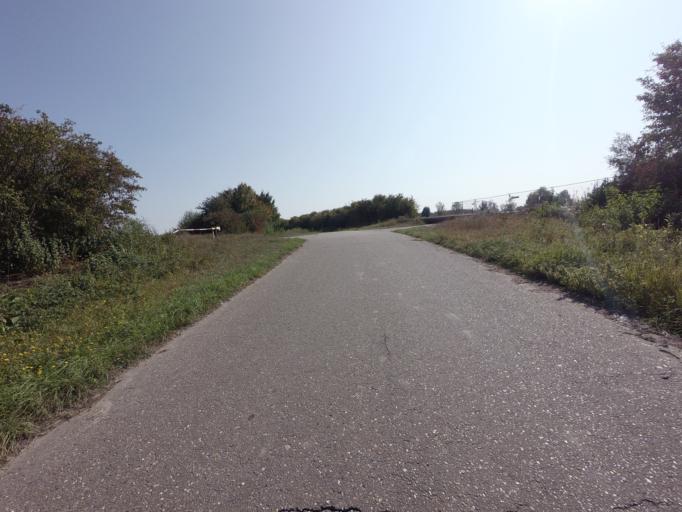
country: NL
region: Limburg
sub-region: Gemeente Maasgouw
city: Maasbracht
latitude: 51.1550
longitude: 5.8556
